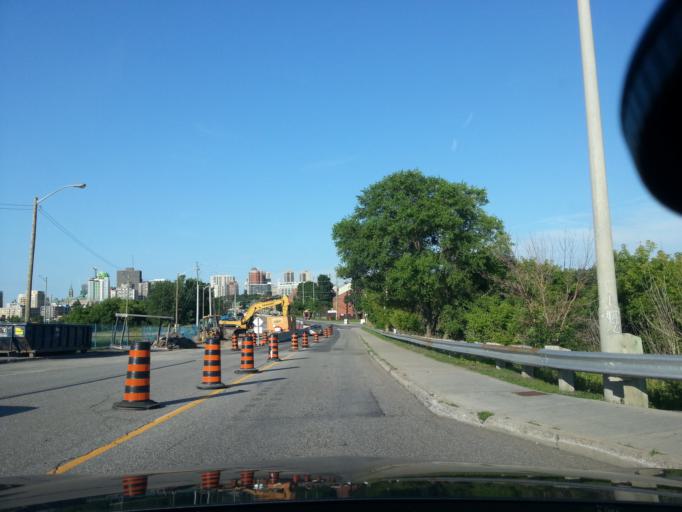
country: CA
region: Ontario
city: Ottawa
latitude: 45.4099
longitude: -75.7201
